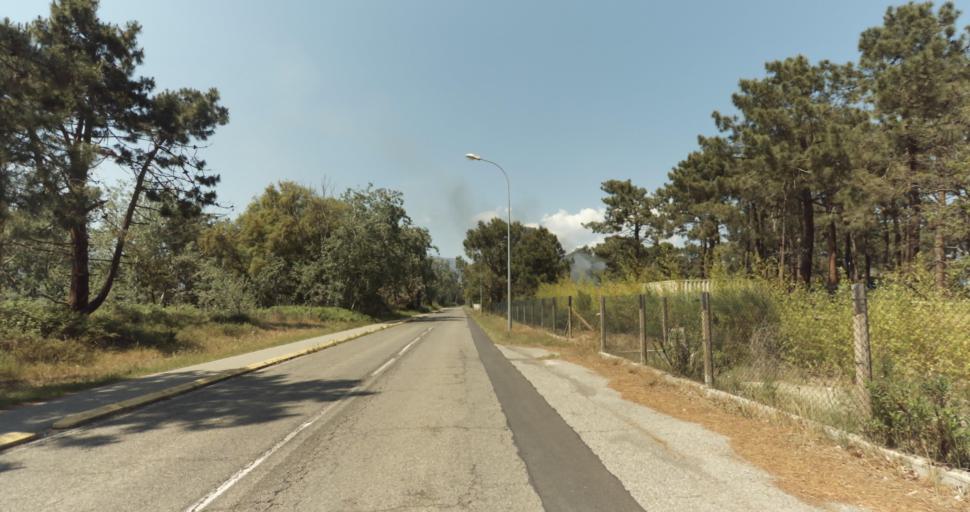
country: FR
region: Corsica
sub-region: Departement de la Haute-Corse
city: Biguglia
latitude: 42.6311
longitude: 9.4653
